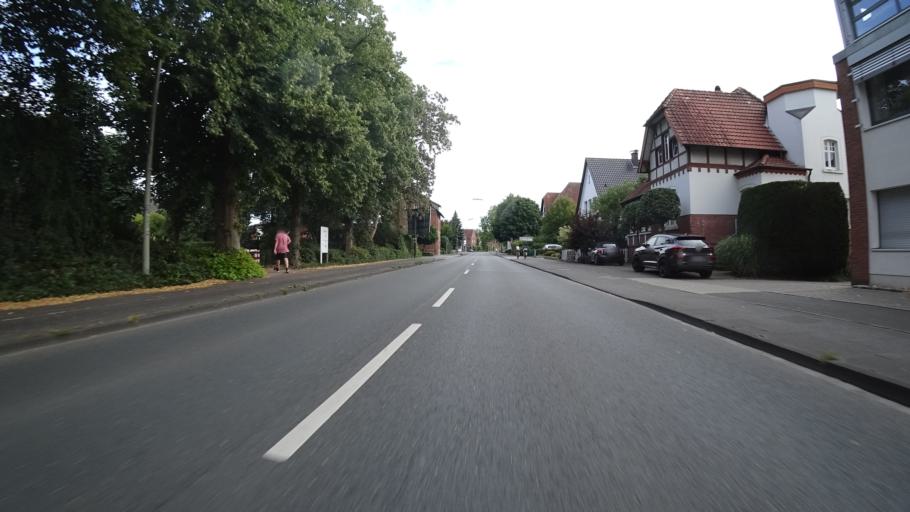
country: DE
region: North Rhine-Westphalia
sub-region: Regierungsbezirk Munster
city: Warendorf
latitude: 51.9487
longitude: 7.9874
